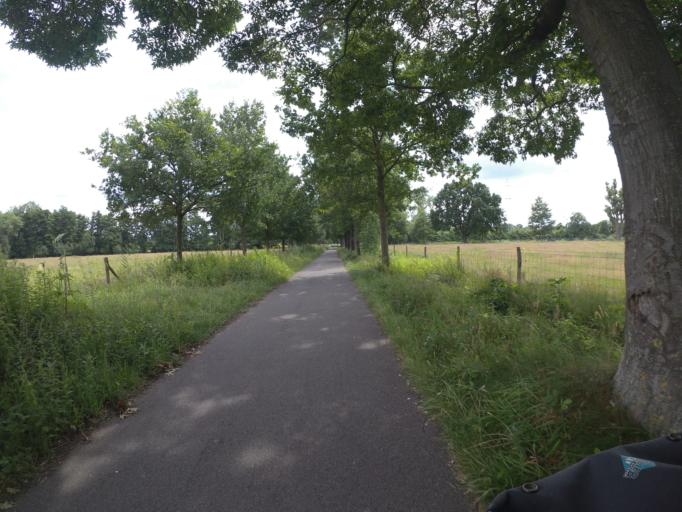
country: NL
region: North Brabant
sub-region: Gemeente Eindhoven
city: Muschberg en Geestenberg
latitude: 51.4360
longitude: 5.5361
